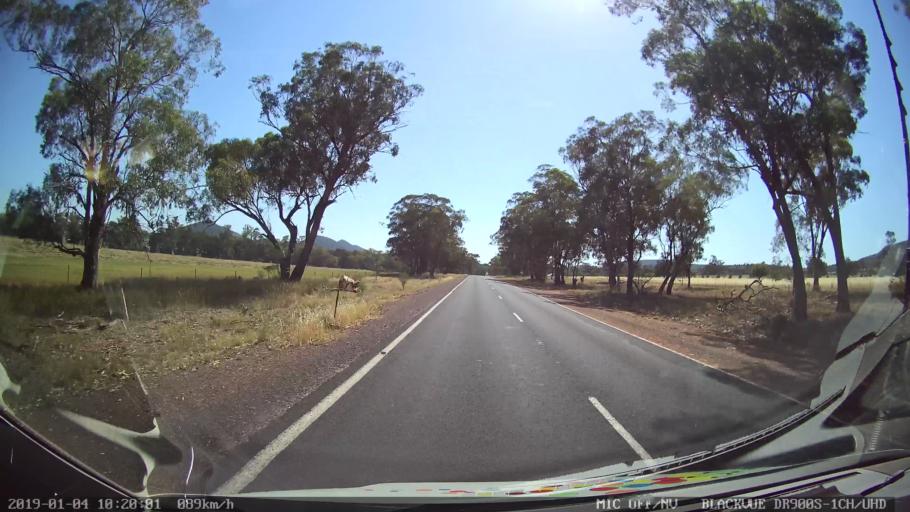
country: AU
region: New South Wales
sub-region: Cabonne
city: Canowindra
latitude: -33.3739
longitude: 148.4894
